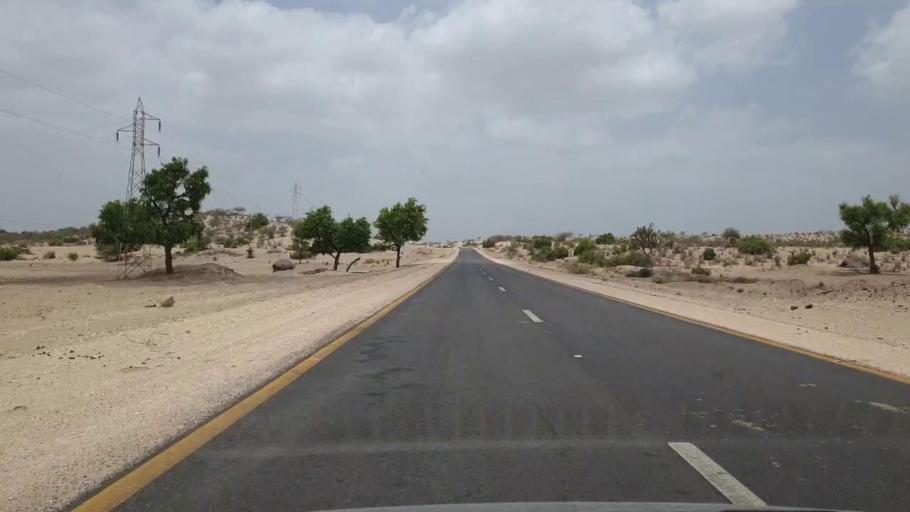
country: PK
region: Sindh
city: Naukot
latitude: 24.8466
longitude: 69.5276
